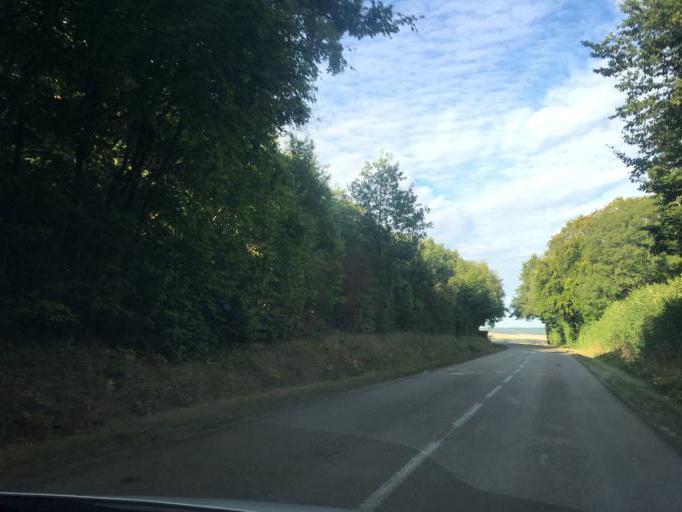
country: FR
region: Bourgogne
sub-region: Departement de l'Yonne
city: Fontenailles
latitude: 47.5794
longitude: 3.4610
